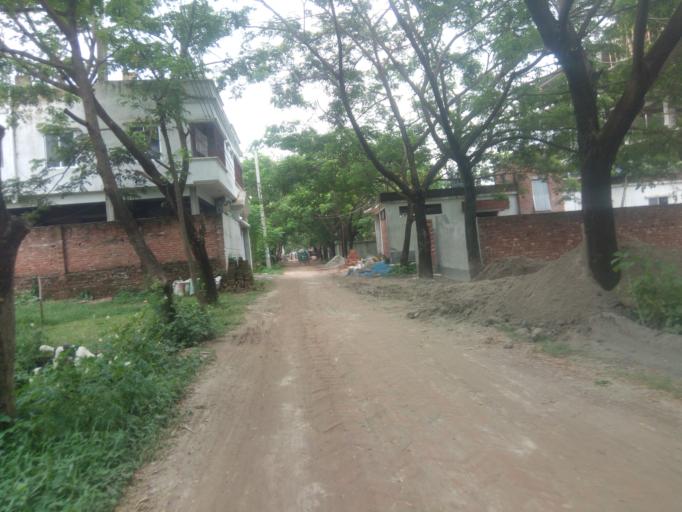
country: BD
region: Dhaka
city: Azimpur
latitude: 23.7528
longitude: 90.3459
